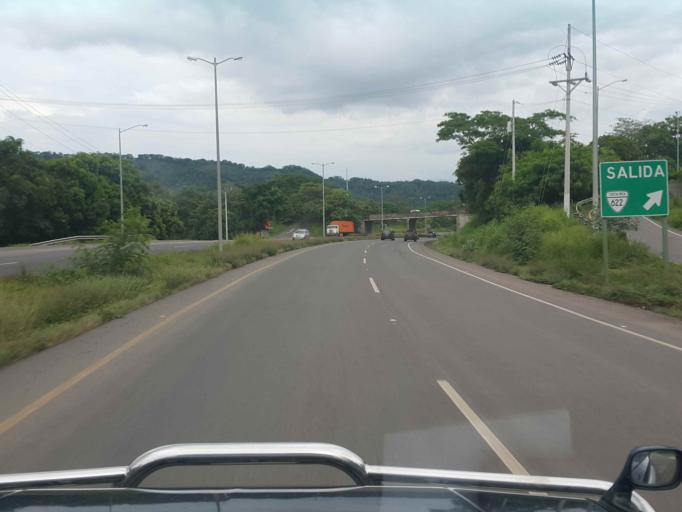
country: CR
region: Puntarenas
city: Esparza
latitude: 9.9201
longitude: -84.6959
